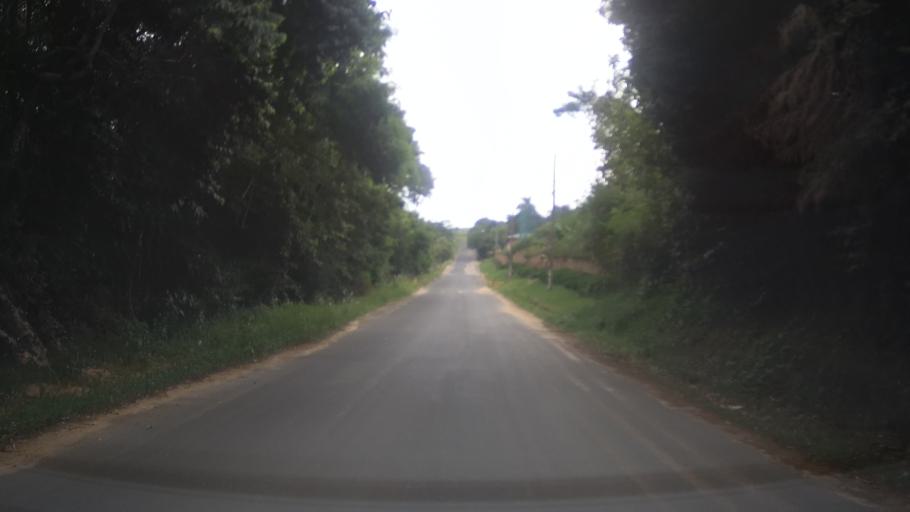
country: BR
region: Sao Paulo
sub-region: Itupeva
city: Itupeva
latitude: -23.1873
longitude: -47.0879
